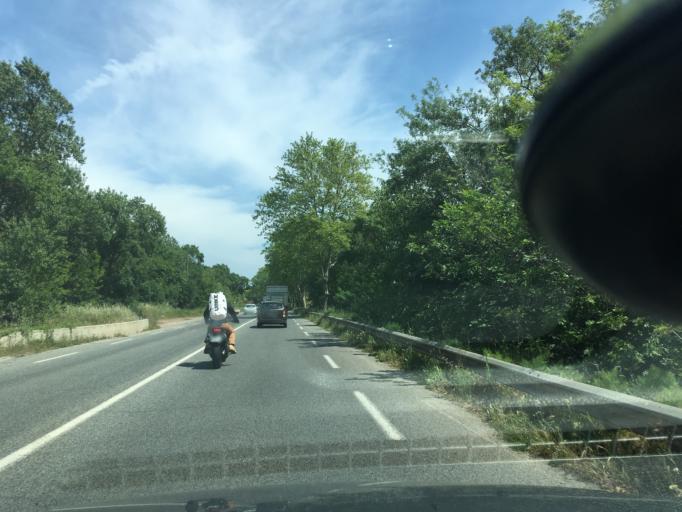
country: FR
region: Provence-Alpes-Cote d'Azur
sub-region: Departement du Var
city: Roquebrune-sur-Argens
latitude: 43.4620
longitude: 6.6507
